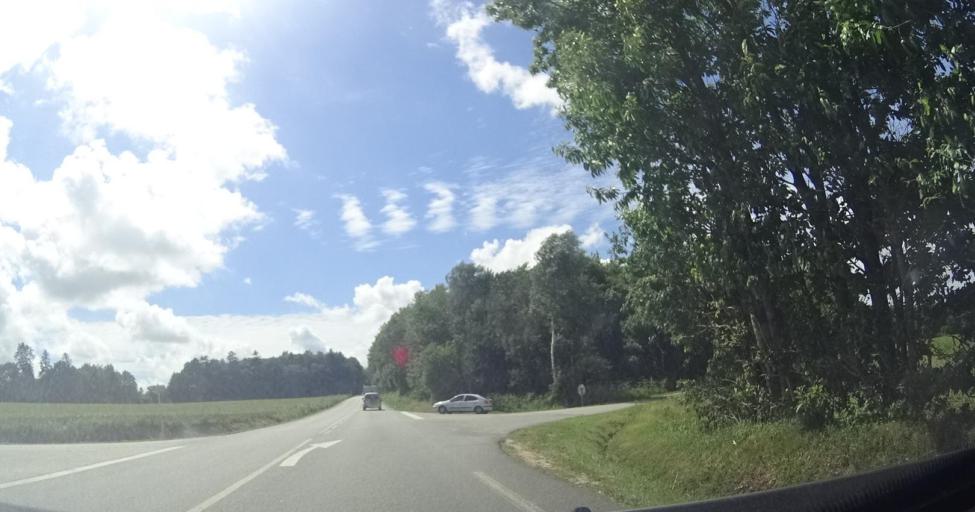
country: FR
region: Brittany
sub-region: Departement du Morbihan
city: Trefflean
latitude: 47.6921
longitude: -2.6006
